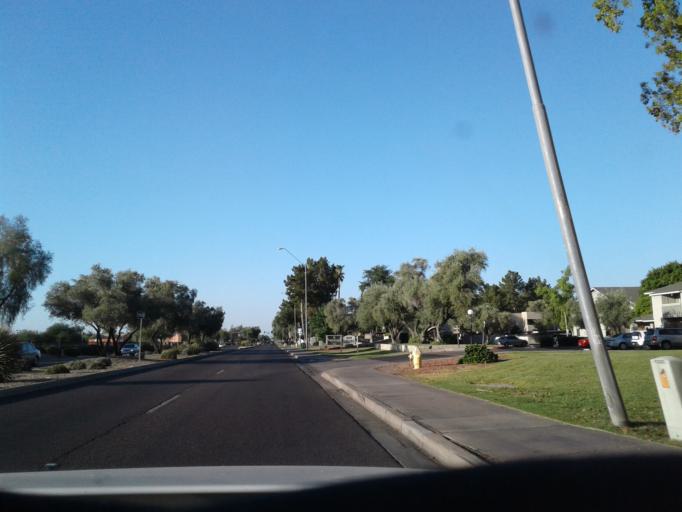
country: US
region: Arizona
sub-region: Maricopa County
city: Peoria
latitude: 33.6238
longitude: -112.1858
